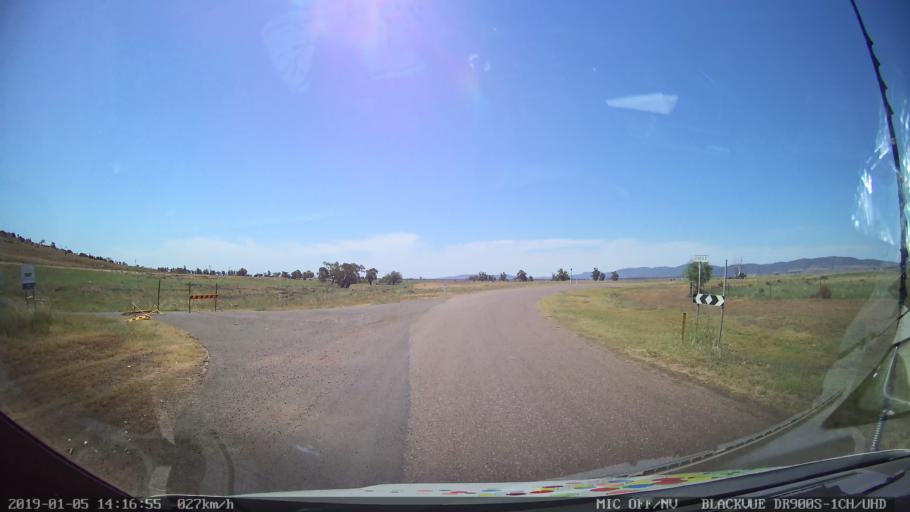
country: AU
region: New South Wales
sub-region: Liverpool Plains
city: Quirindi
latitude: -31.2562
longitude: 150.4741
